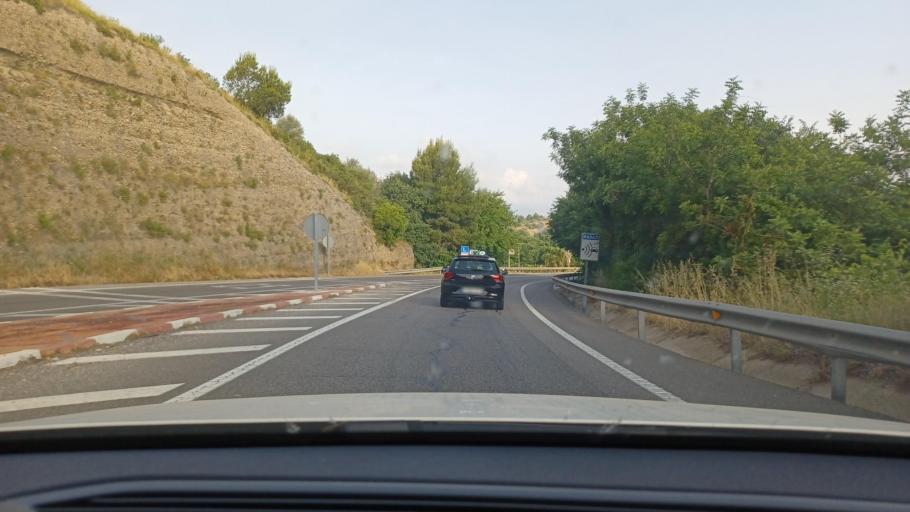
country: ES
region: Catalonia
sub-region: Provincia de Tarragona
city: Tortosa
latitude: 40.7759
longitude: 0.5103
